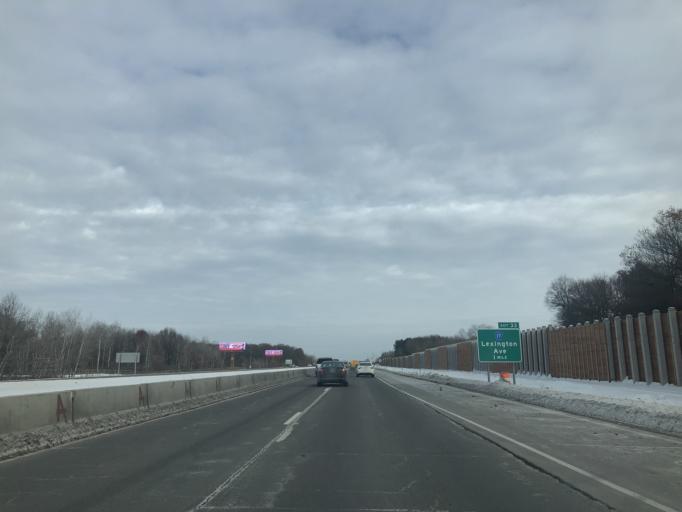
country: US
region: Minnesota
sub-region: Anoka County
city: Lexington
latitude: 45.1475
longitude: -93.1795
